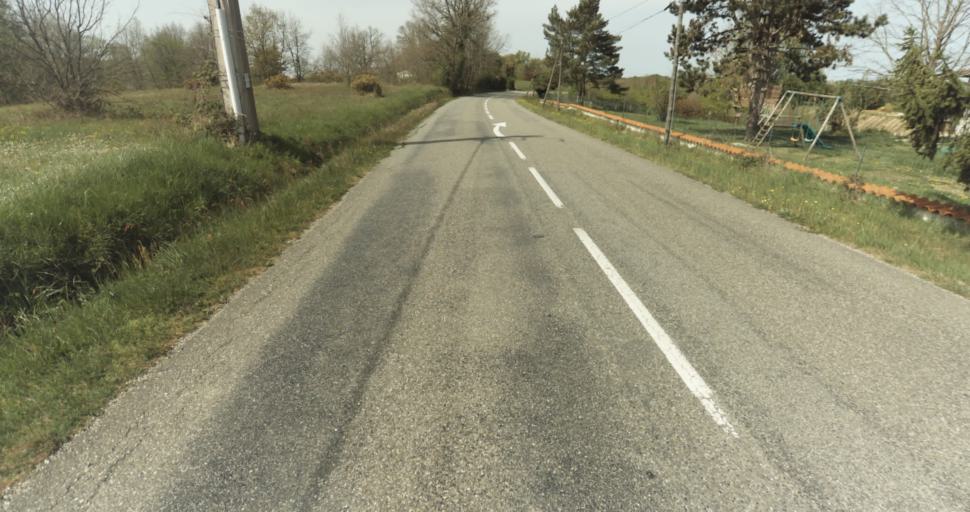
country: FR
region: Midi-Pyrenees
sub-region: Departement du Tarn-et-Garonne
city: Moissac
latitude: 44.1667
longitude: 1.0882
